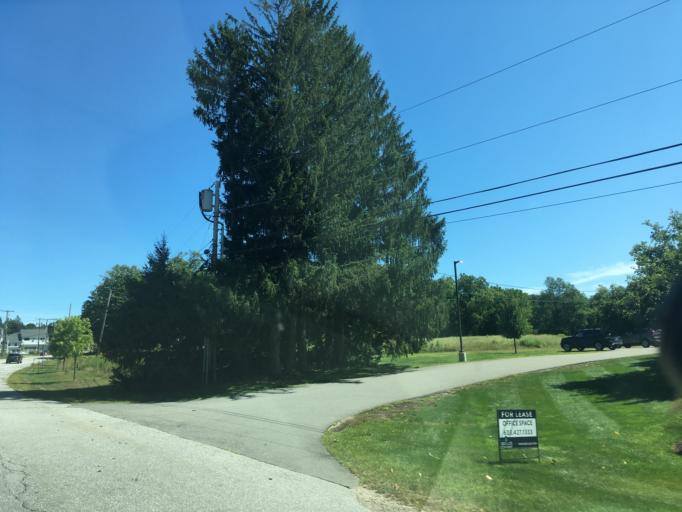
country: US
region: New Hampshire
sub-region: Rockingham County
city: Stratham Station
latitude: 43.0230
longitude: -70.9150
